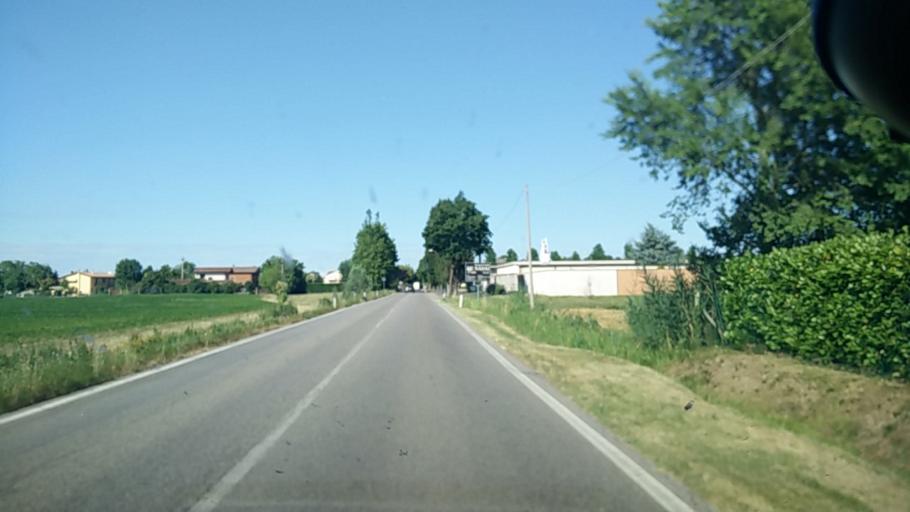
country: IT
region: Veneto
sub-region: Provincia di Treviso
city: Mignagola
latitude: 45.6865
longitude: 12.3145
